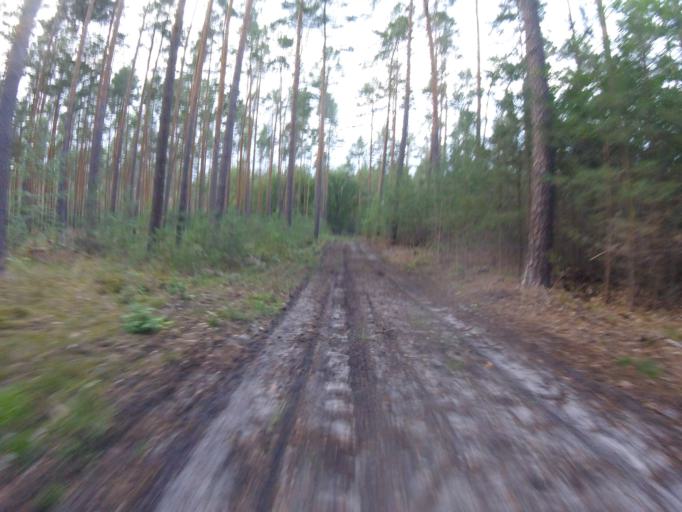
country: DE
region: Brandenburg
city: Gross Koris
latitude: 52.2020
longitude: 13.6863
